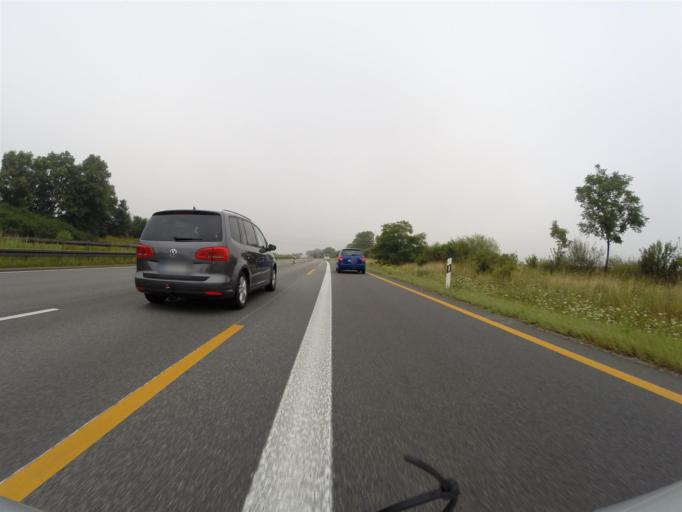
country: DE
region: Thuringia
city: Schwabhausen
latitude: 50.9002
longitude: 10.7438
